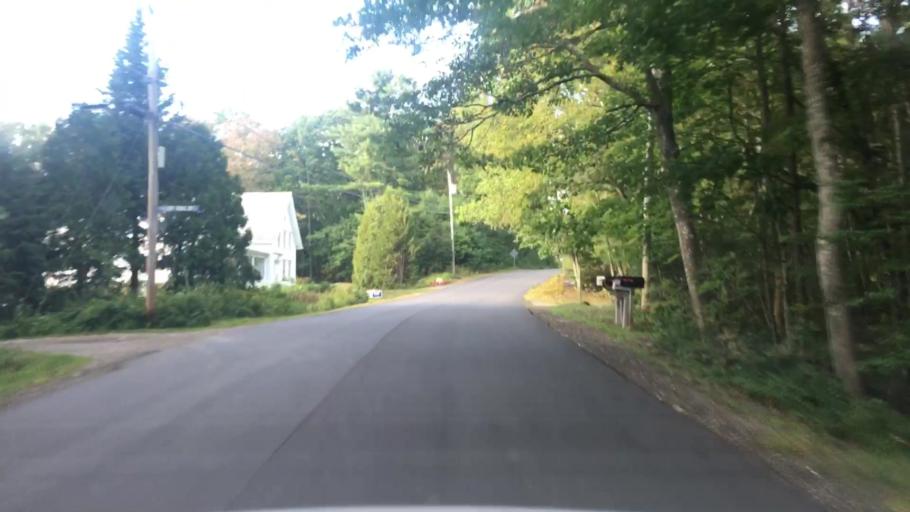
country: US
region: Maine
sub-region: Lincoln County
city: Boothbay
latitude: 43.9073
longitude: -69.6556
